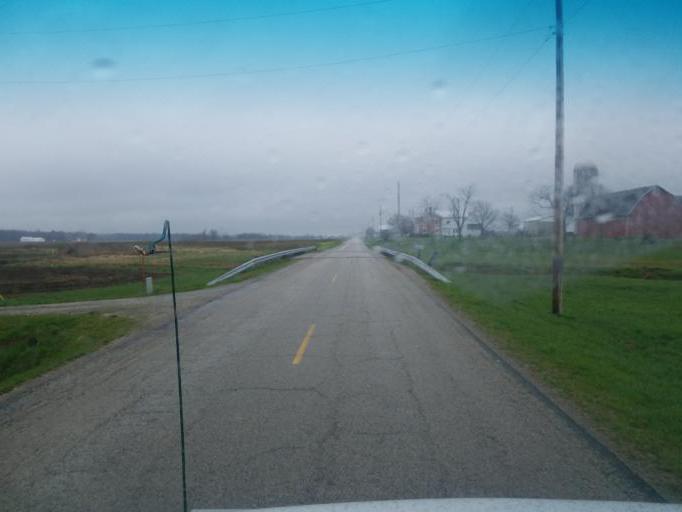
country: US
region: Ohio
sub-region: Crawford County
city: Bucyrus
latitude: 40.9649
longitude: -82.9877
